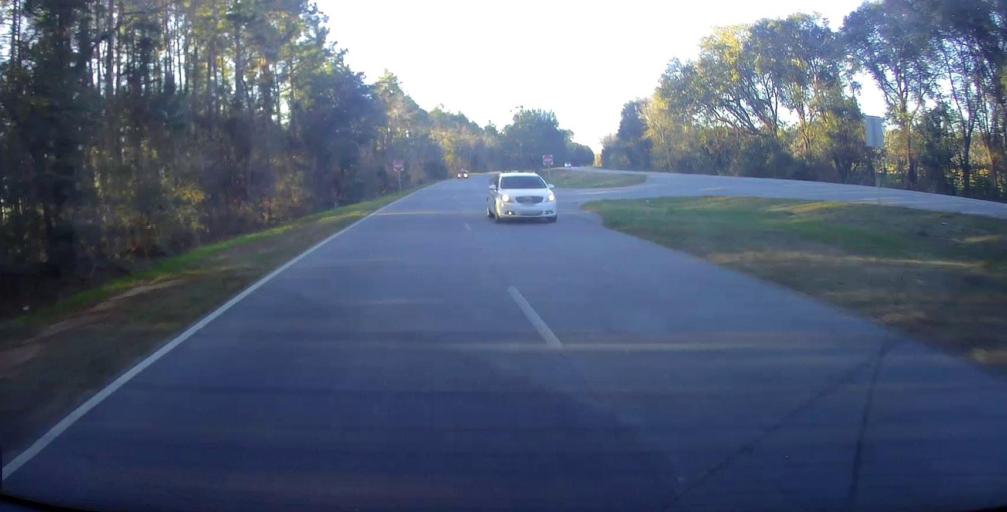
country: US
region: Georgia
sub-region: Dougherty County
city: Albany
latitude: 31.5373
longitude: -84.2223
